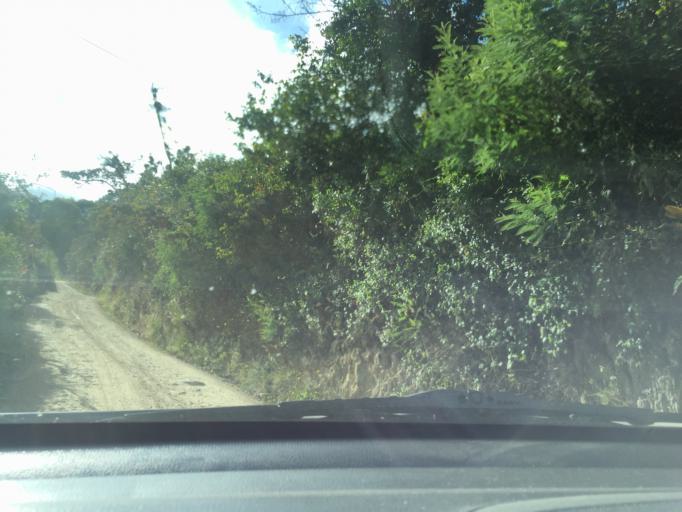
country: CO
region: Cundinamarca
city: Sopo
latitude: 4.9206
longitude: -73.9113
